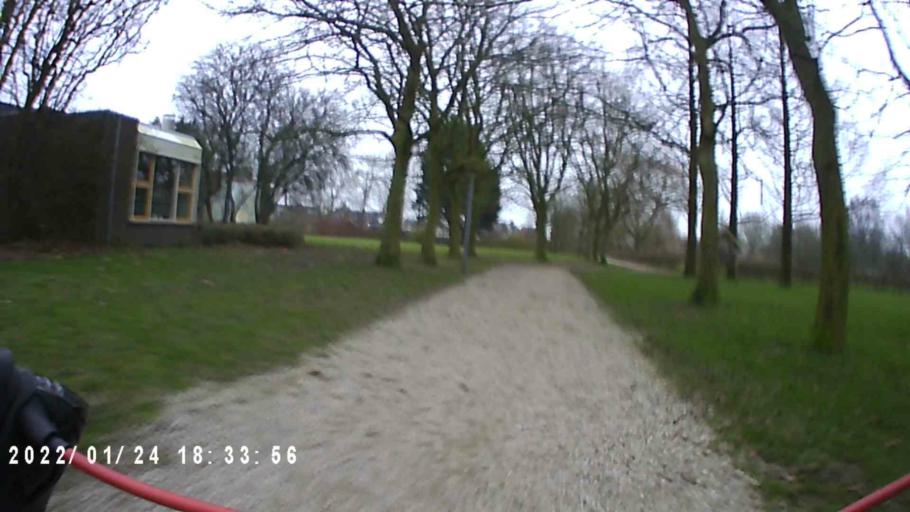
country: NL
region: Groningen
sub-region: Gemeente De Marne
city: Ulrum
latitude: 53.3564
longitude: 6.3360
